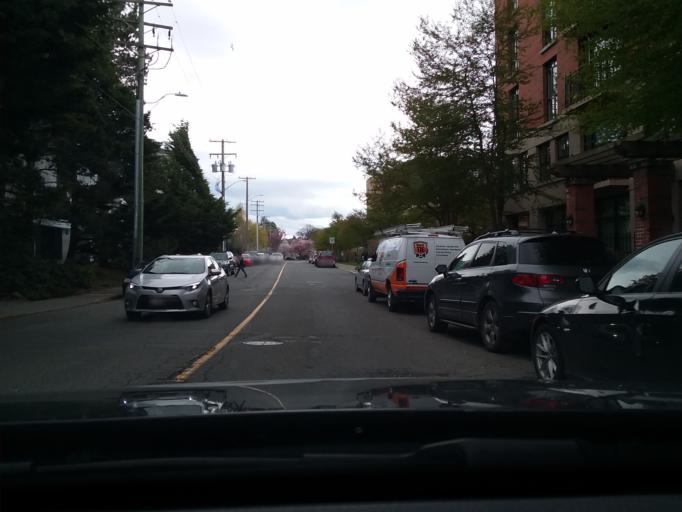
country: CA
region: British Columbia
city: Victoria
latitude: 48.4208
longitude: -123.3625
